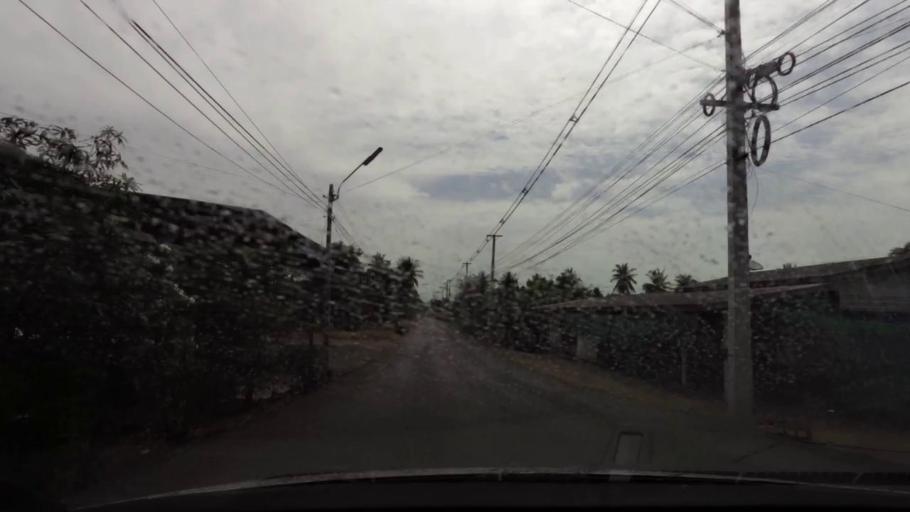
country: TH
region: Ratchaburi
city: Damnoen Saduak
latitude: 13.5345
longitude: 99.9868
